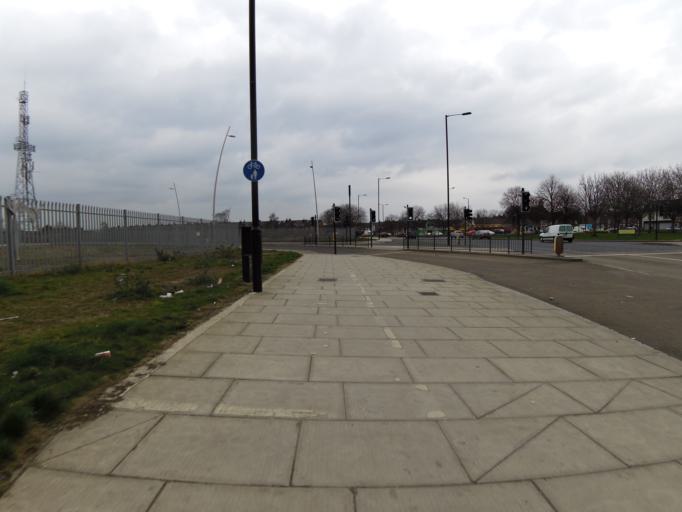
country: GB
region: England
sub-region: Doncaster
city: Doncaster
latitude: 53.5284
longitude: -1.1289
